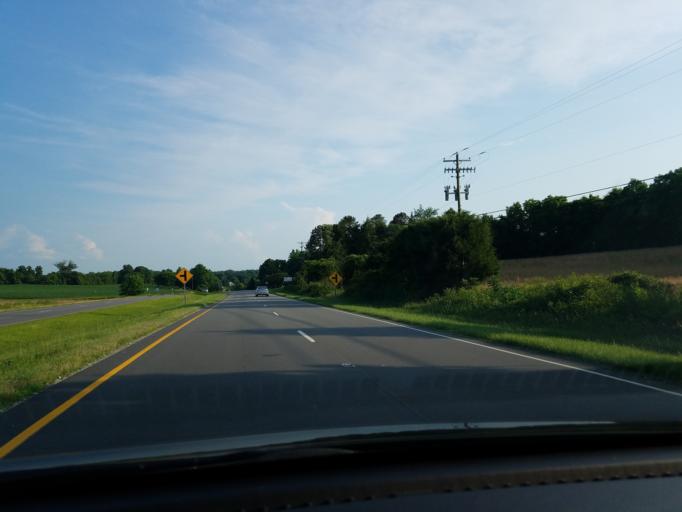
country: US
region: North Carolina
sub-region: Durham County
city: Gorman
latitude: 36.1473
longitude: -78.9048
